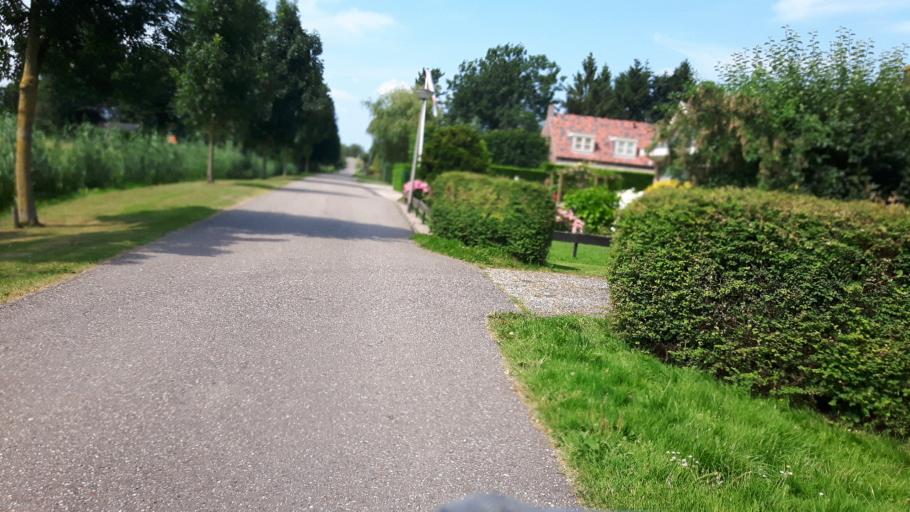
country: NL
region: South Holland
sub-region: Molenwaard
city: Liesveld
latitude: 51.9316
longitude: 4.8335
